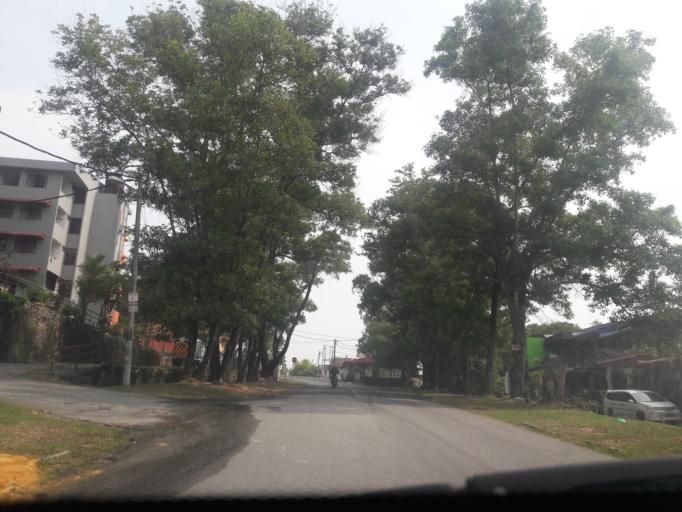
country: MY
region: Kedah
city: Kulim
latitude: 5.3629
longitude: 100.5378
